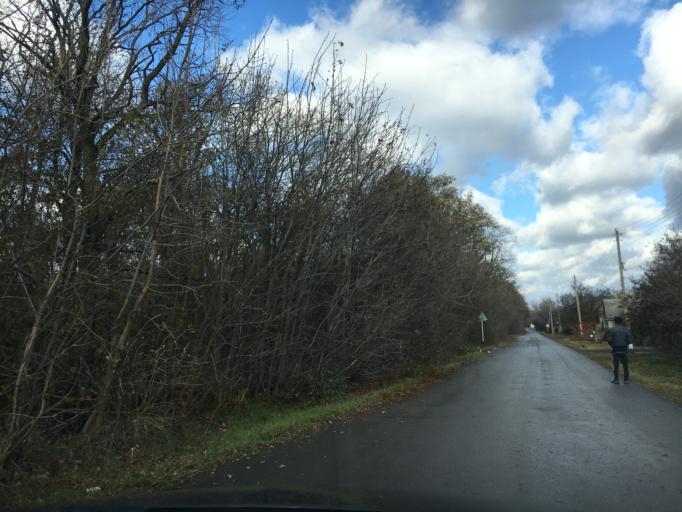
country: RU
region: Rostov
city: Pokrovskoye
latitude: 47.4827
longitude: 38.9131
